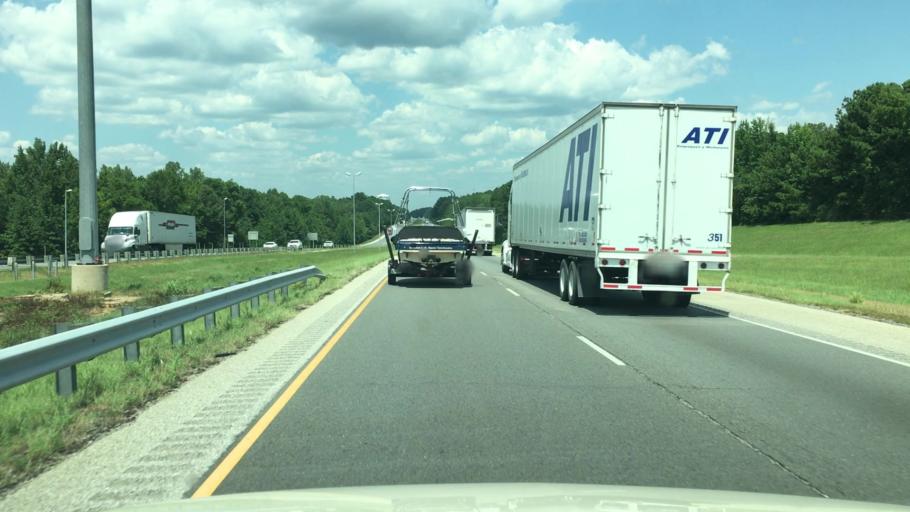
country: US
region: Arkansas
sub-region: Clark County
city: Arkadelphia
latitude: 34.1203
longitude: -93.0919
